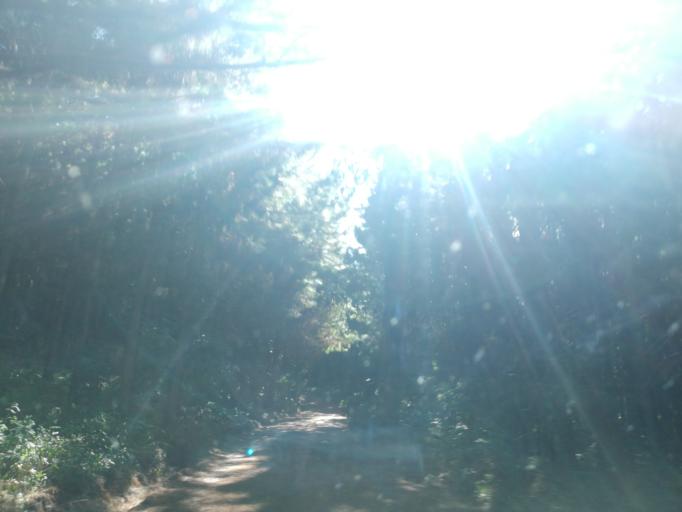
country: AR
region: Misiones
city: Dos de Mayo
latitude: -27.0166
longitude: -54.4176
